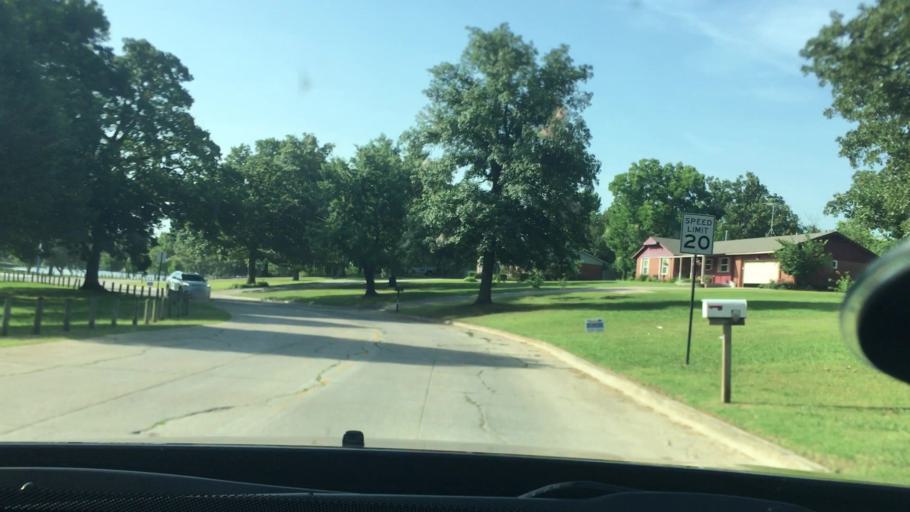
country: US
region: Oklahoma
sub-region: Pontotoc County
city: Ada
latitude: 34.7669
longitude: -96.6575
